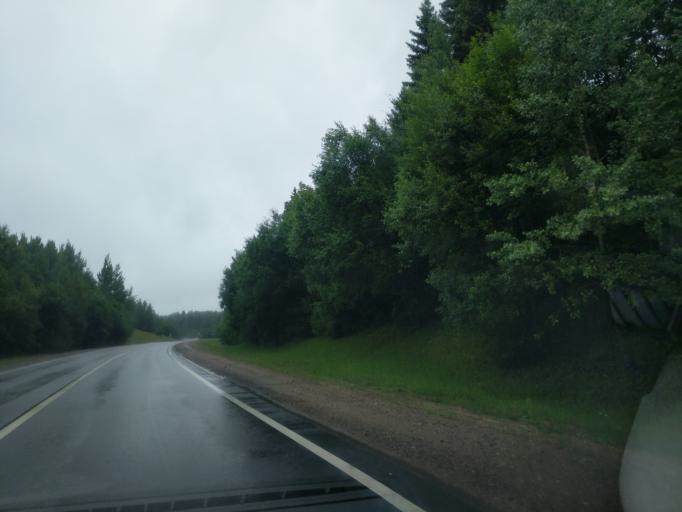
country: BY
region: Minsk
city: Bal'shavik
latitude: 54.1070
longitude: 27.5292
